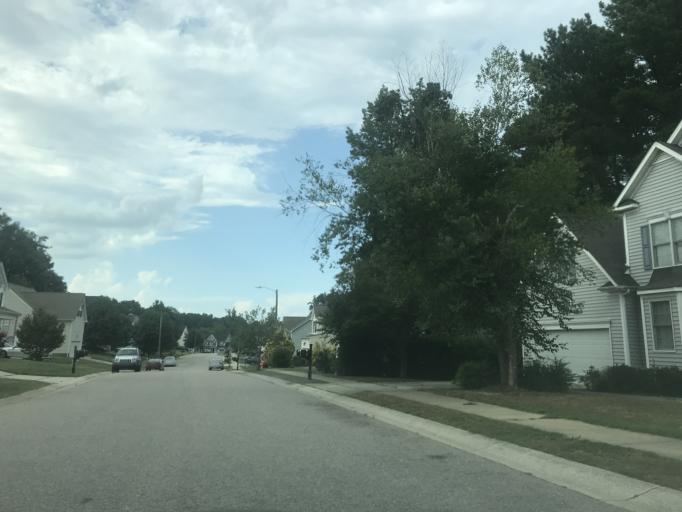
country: US
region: North Carolina
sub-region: Wake County
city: Knightdale
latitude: 35.8389
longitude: -78.5568
